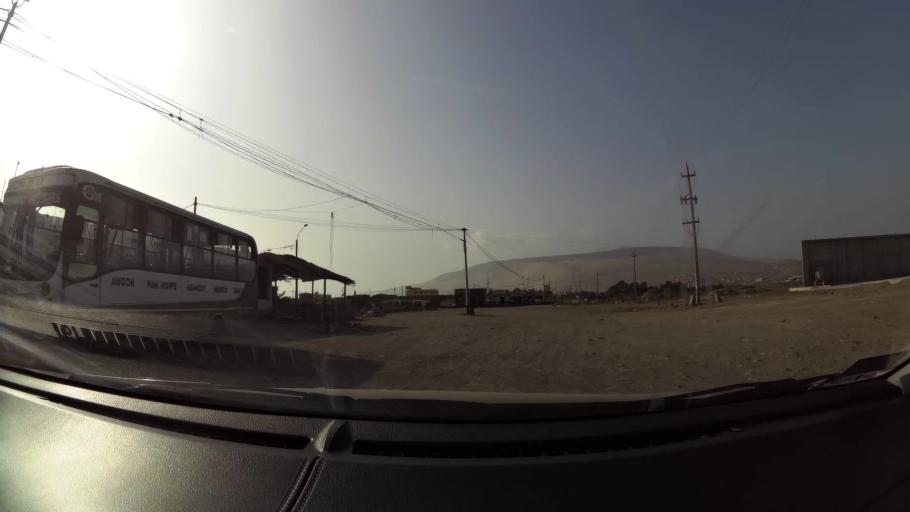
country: PE
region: Lima
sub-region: Lima
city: Santa Rosa
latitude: -11.7603
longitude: -77.1697
